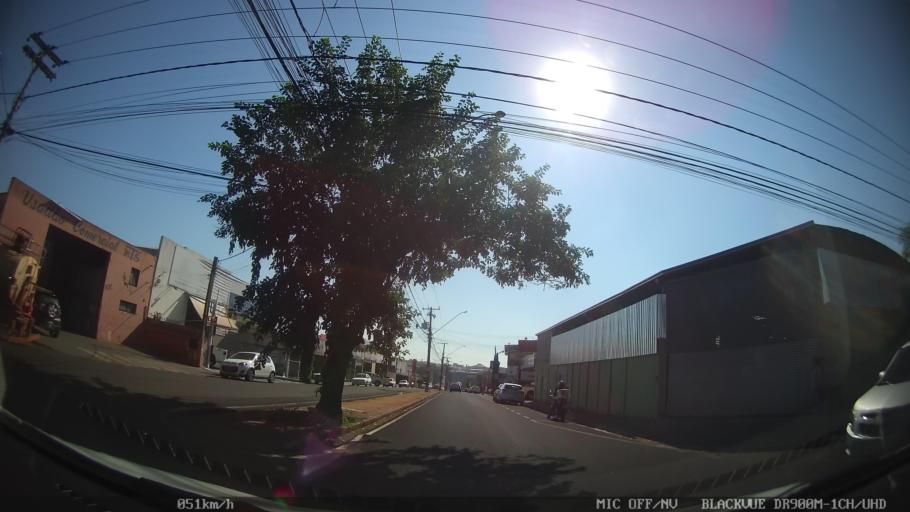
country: BR
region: Sao Paulo
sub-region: Sao Jose Do Rio Preto
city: Sao Jose do Rio Preto
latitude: -20.7815
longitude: -49.3867
